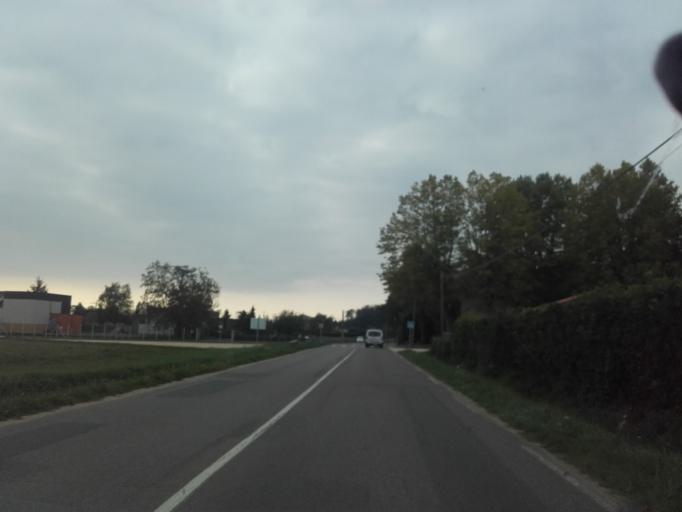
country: FR
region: Bourgogne
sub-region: Departement de Saone-et-Loire
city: Creches-sur-Saone
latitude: 46.2564
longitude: 4.7816
